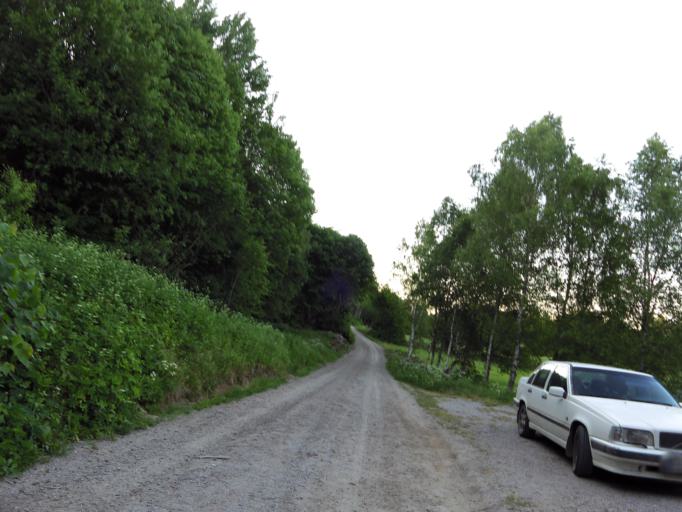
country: SE
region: Blekinge
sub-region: Olofstroms Kommun
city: Olofstroem
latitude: 56.4123
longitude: 14.5612
